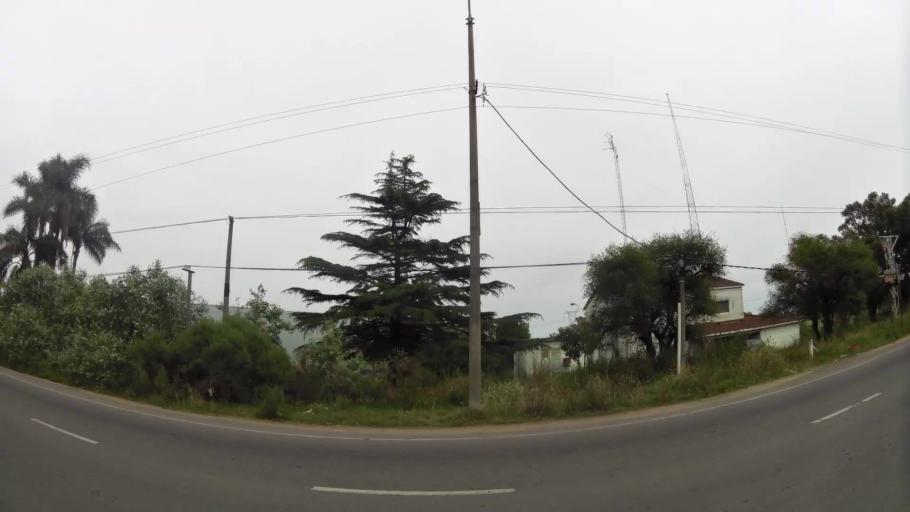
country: UY
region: Canelones
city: La Paz
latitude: -34.7744
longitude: -56.2262
